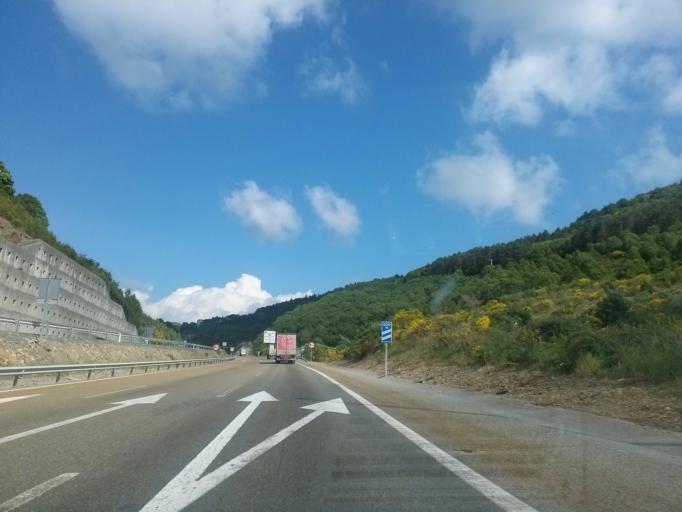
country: ES
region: Castille and Leon
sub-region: Provincia de Leon
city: Balboa
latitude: 42.7281
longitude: -7.0377
